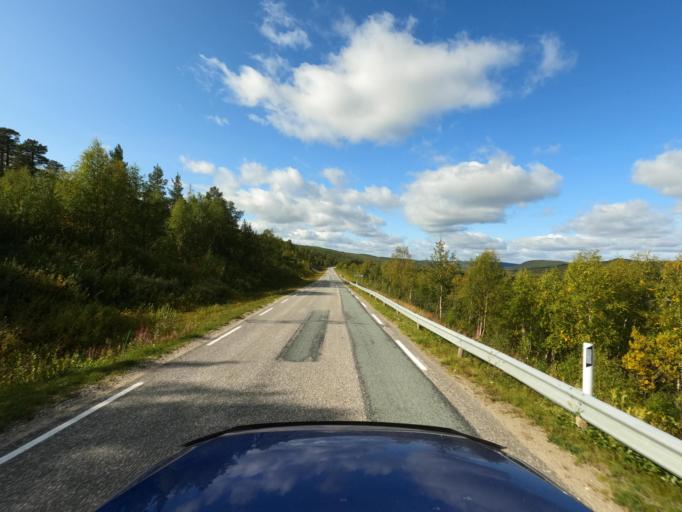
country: NO
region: Finnmark Fylke
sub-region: Karasjok
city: Karasjohka
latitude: 69.4352
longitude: 25.7051
